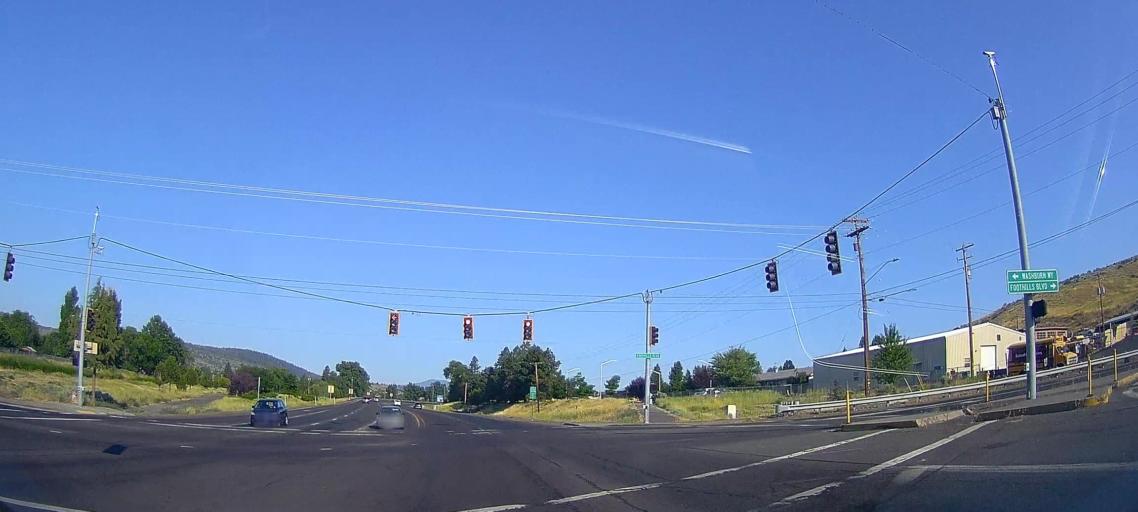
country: US
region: Oregon
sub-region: Klamath County
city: Klamath Falls
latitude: 42.2249
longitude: -121.7570
